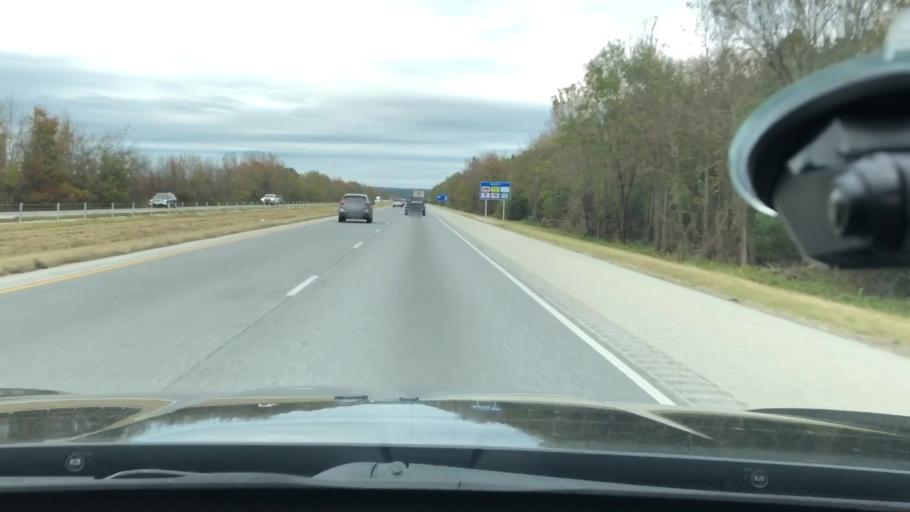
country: US
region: Arkansas
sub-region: Clark County
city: Arkadelphia
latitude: 34.1602
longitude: -93.0768
